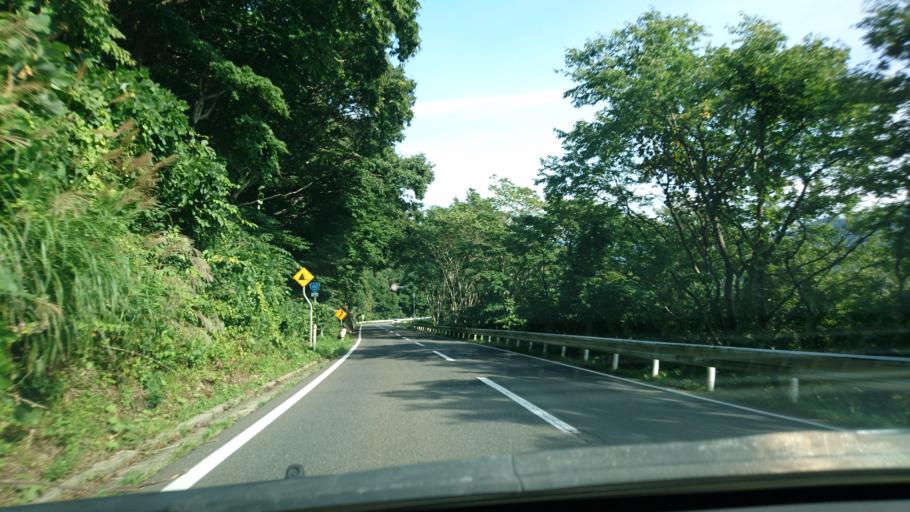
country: JP
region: Iwate
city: Kitakami
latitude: 39.3084
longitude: 140.8482
